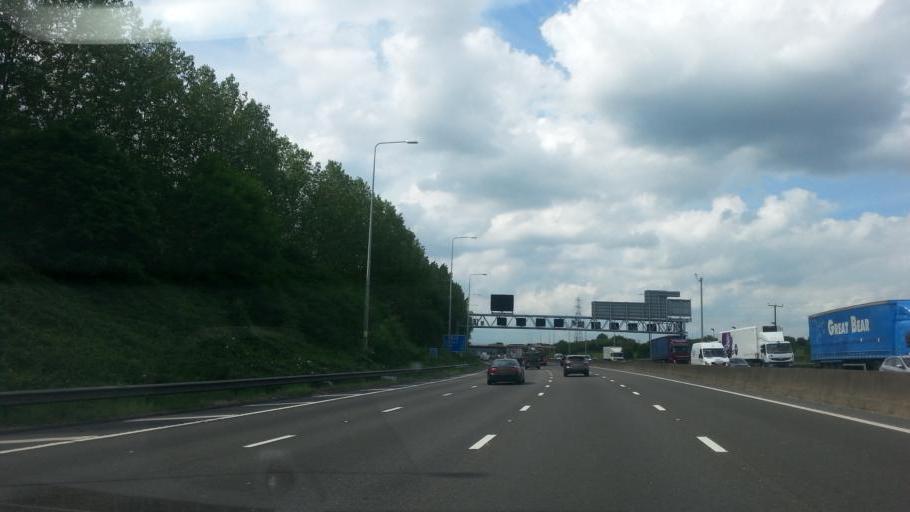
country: GB
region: England
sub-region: Kirklees
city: Cleckheaton
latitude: 53.7038
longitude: -1.7433
